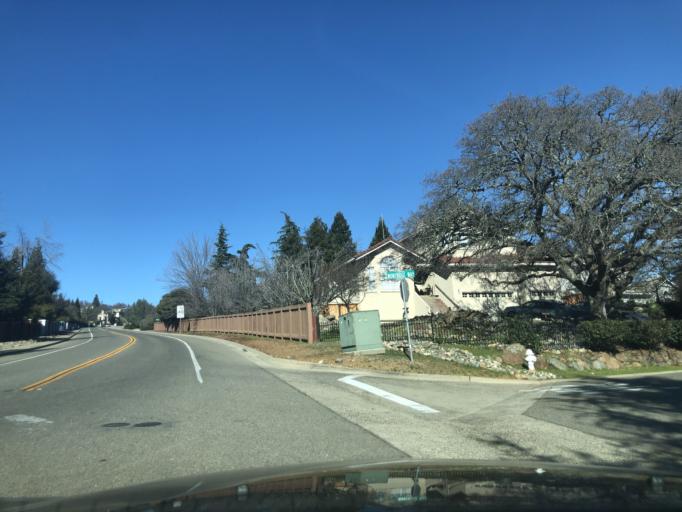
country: US
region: California
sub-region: El Dorado County
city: El Dorado Hills
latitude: 38.6580
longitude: -121.0833
